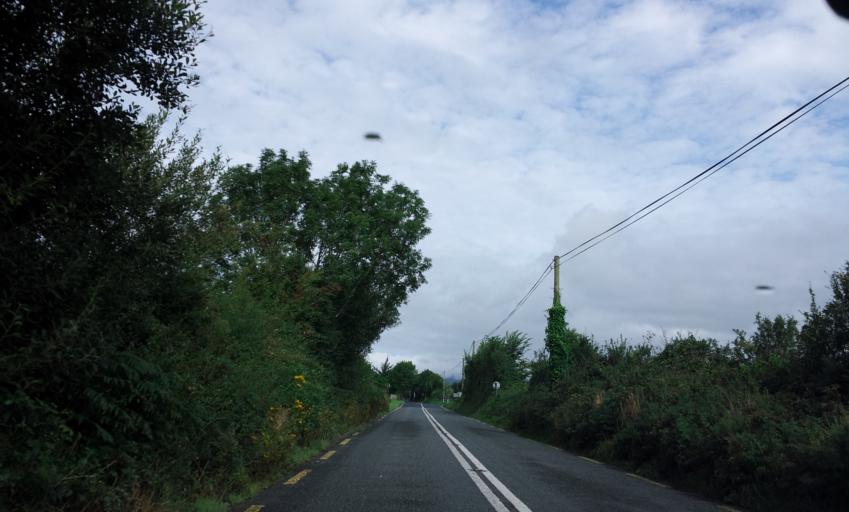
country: IE
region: Munster
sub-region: Ciarrai
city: Killorglin
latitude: 52.0912
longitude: -9.6911
